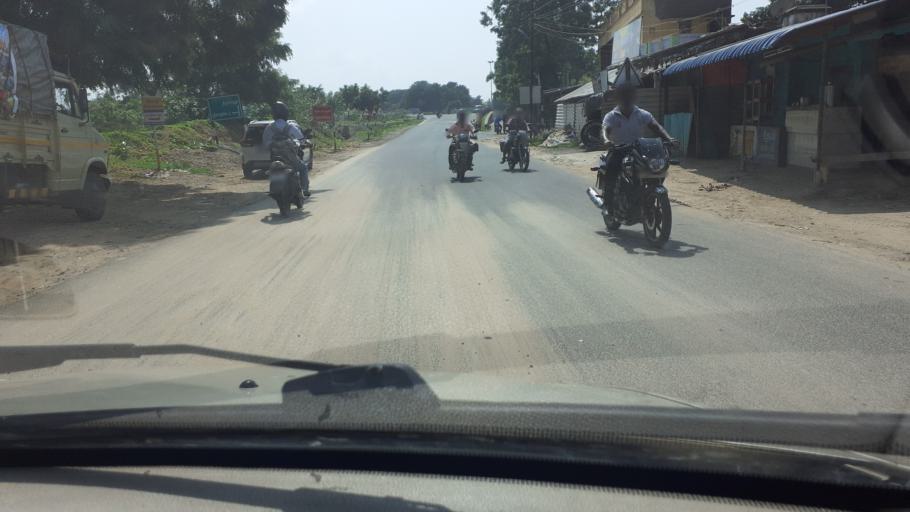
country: IN
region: Tamil Nadu
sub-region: Thoothukkudi
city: Srivaikuntam
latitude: 8.6241
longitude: 77.9092
